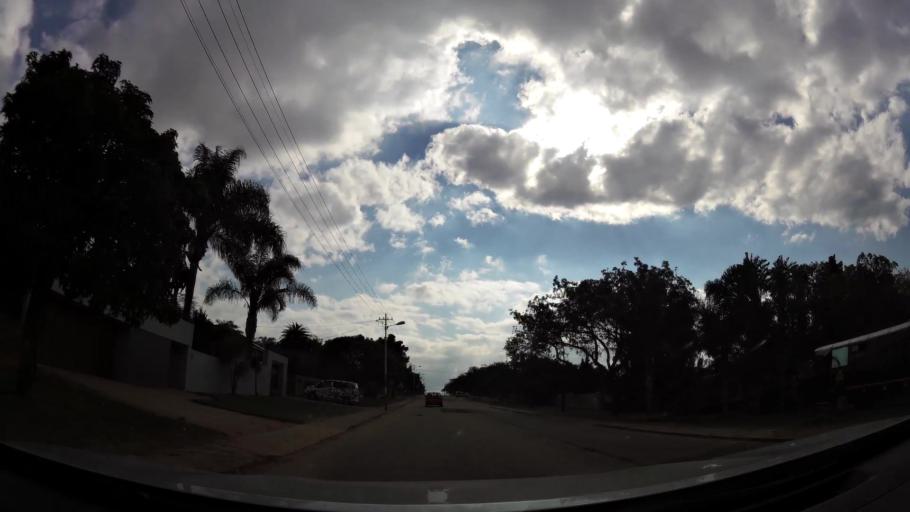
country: ZA
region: Eastern Cape
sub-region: Nelson Mandela Bay Metropolitan Municipality
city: Uitenhage
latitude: -33.7512
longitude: 25.4086
